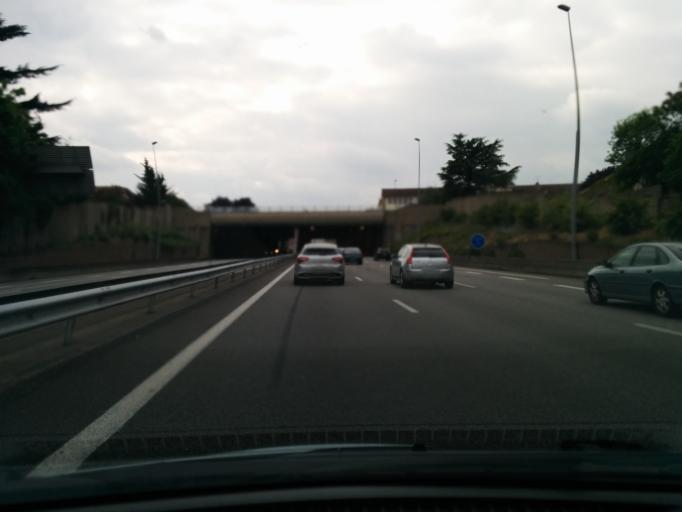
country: FR
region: Ile-de-France
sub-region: Departement des Yvelines
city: Mantes-la-Jolie
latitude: 48.9772
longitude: 1.7155
